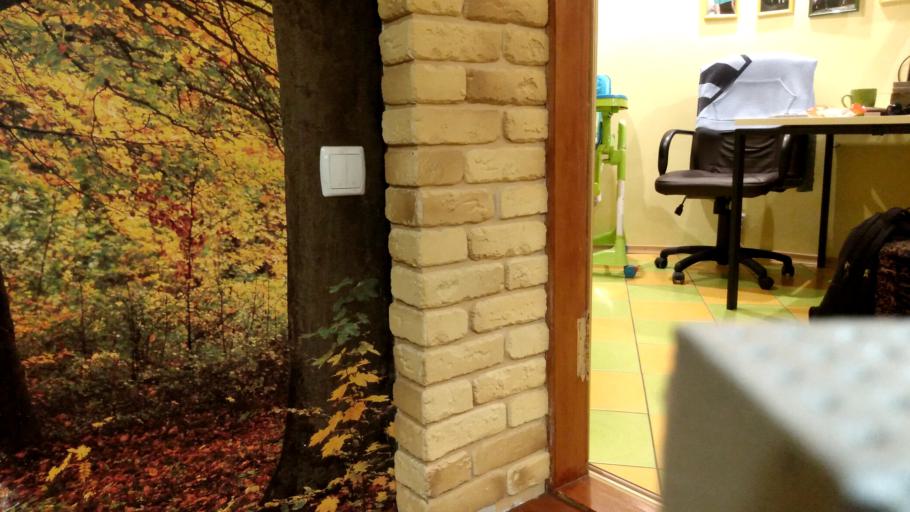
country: RU
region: Republic of Karelia
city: Pudozh
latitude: 61.8046
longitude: 37.6701
